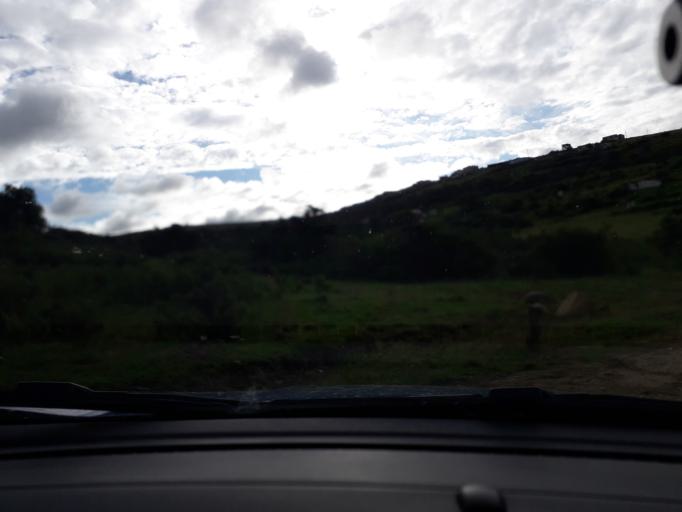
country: ZA
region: Eastern Cape
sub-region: Buffalo City Metropolitan Municipality
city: East London
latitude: -32.8029
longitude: 27.9608
